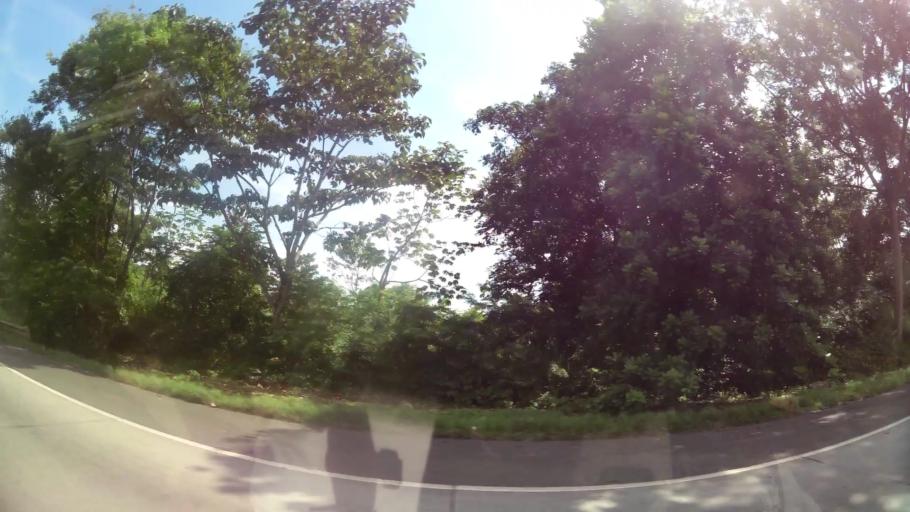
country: PA
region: Panama
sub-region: Distrito de Panama
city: Paraiso
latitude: 9.0274
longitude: -79.6010
